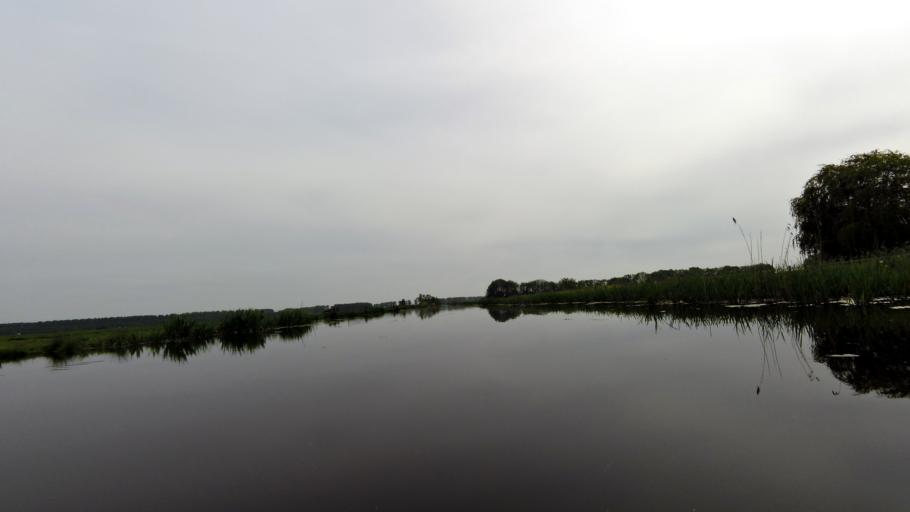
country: NL
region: South Holland
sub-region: Bodegraven-Reeuwijk
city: Reeuwijk
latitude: 52.0729
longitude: 4.7184
